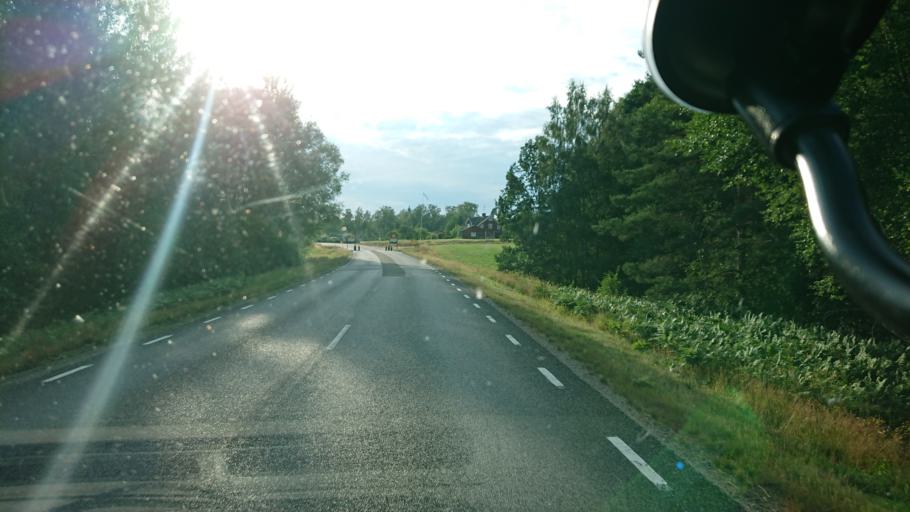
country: SE
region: Kronoberg
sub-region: Vaxjo Kommun
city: Rottne
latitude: 57.0344
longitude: 14.9462
